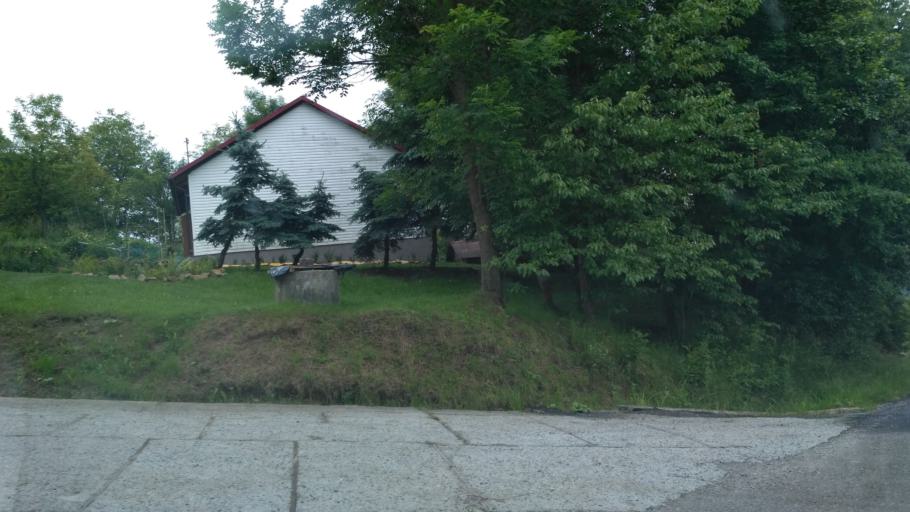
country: PL
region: Subcarpathian Voivodeship
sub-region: Powiat przemyski
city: Nienadowa
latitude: 49.8614
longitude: 22.4095
